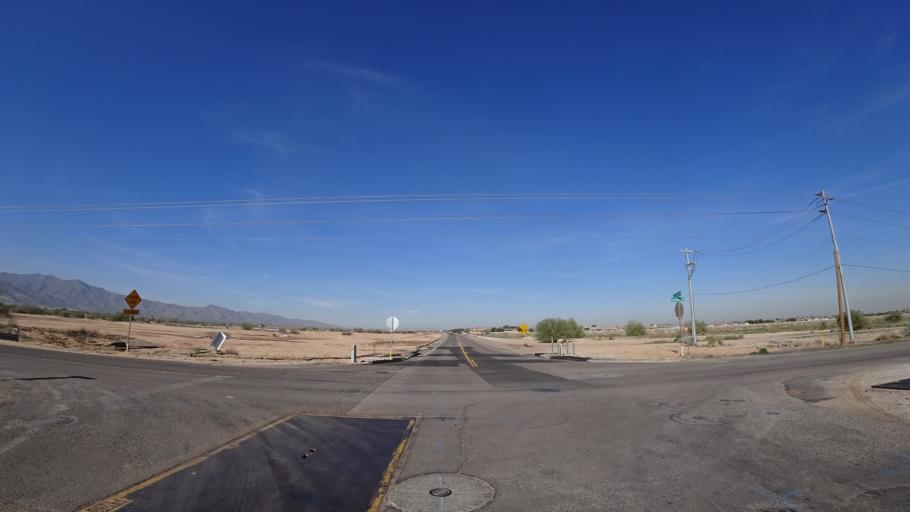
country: US
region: Arizona
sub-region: Maricopa County
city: Citrus Park
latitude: 33.5081
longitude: -112.4615
